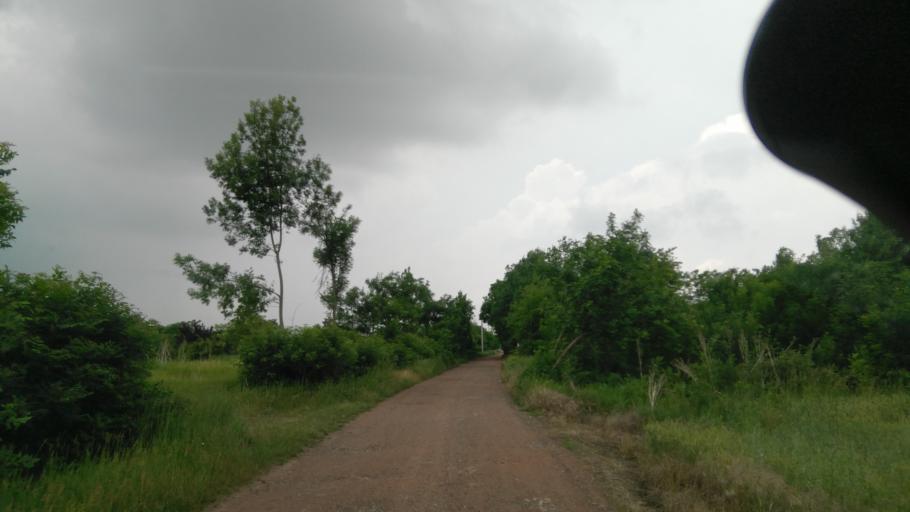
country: HU
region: Bekes
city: Bekescsaba
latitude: 46.7056
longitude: 21.1345
